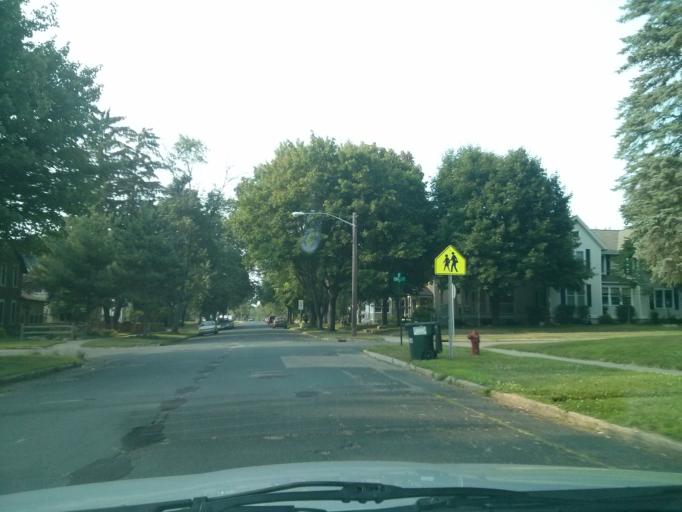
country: US
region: Wisconsin
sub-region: Saint Croix County
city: Hudson
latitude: 44.9811
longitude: -92.7510
